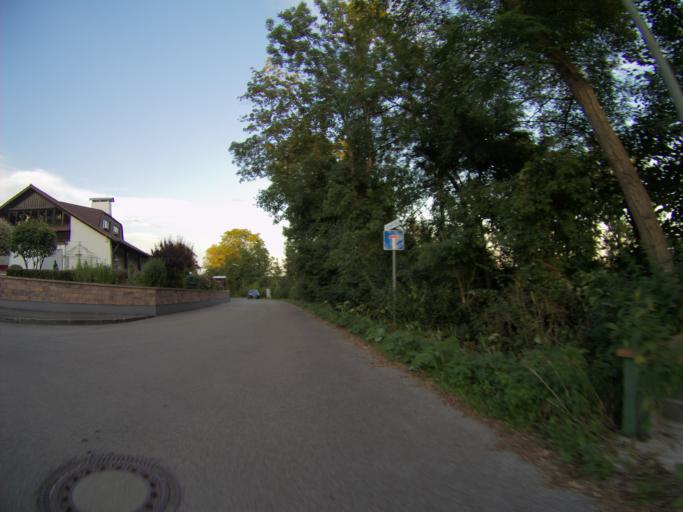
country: DE
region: Bavaria
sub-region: Upper Bavaria
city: Marzling
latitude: 48.4104
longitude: 11.7885
